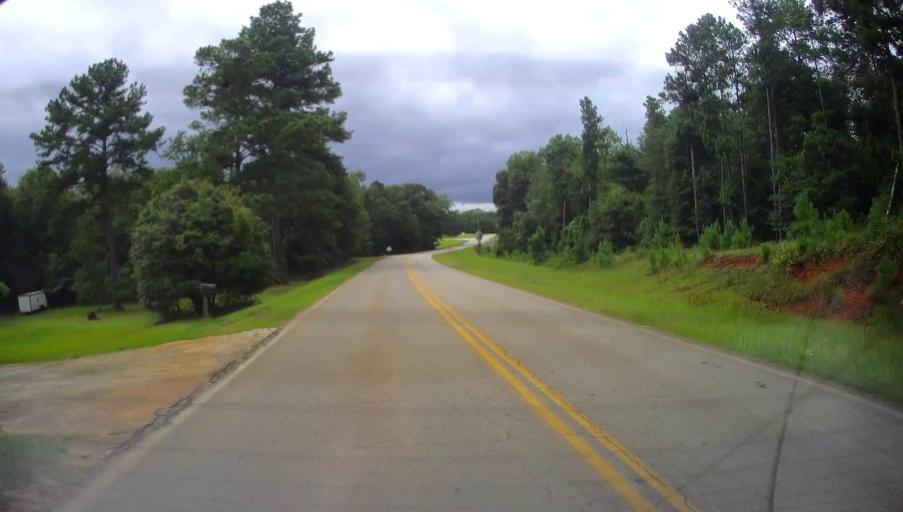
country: US
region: Georgia
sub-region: Twiggs County
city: Jeffersonville
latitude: 32.7604
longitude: -83.4900
